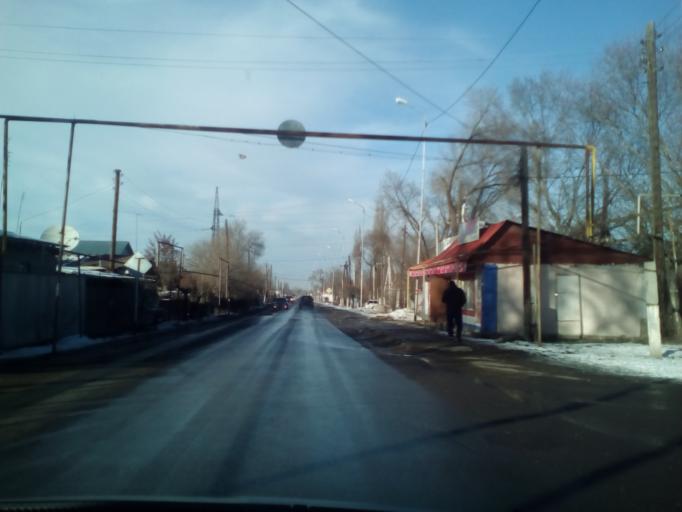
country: KZ
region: Almaty Oblysy
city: Burunday
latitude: 43.1678
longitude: 76.4165
